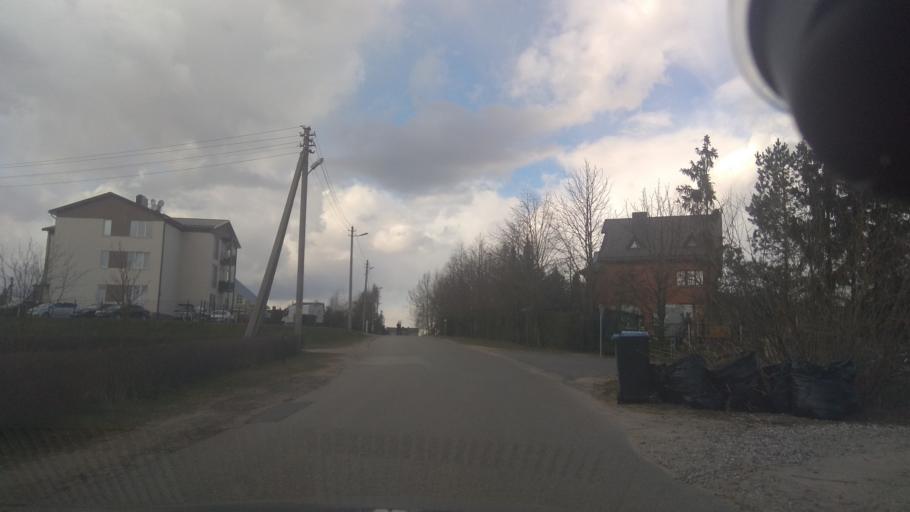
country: LT
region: Vilnius County
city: Pasilaiciai
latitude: 54.7401
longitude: 25.2024
